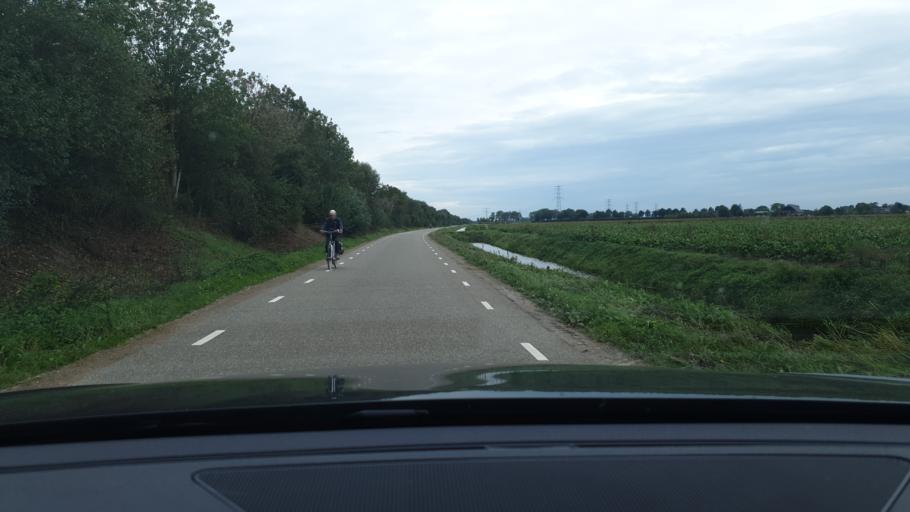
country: NL
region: Gelderland
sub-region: Gemeente Overbetuwe
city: Valburg
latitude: 51.8967
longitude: 5.8081
